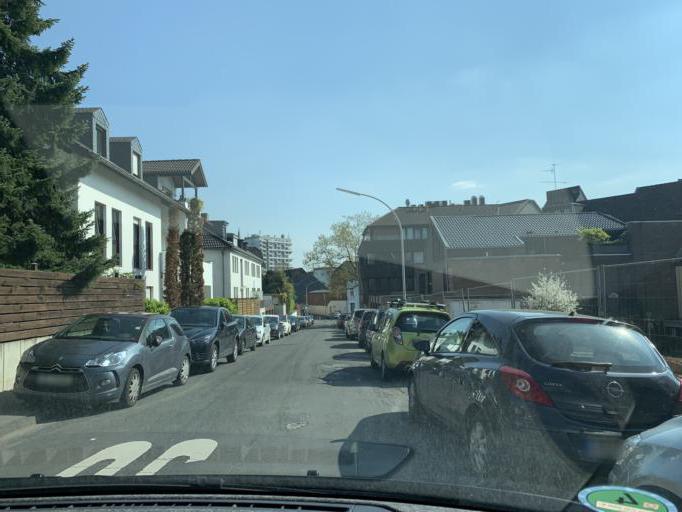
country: DE
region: North Rhine-Westphalia
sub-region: Regierungsbezirk Dusseldorf
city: Monchengladbach
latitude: 51.1343
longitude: 6.4546
